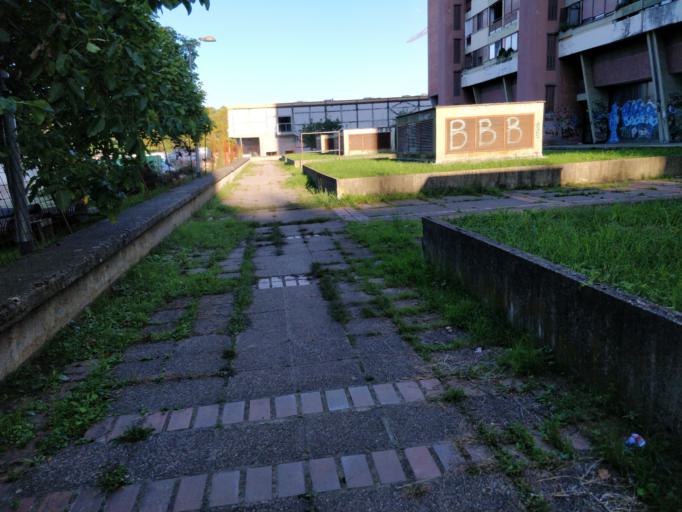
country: HR
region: Grad Zagreb
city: Novi Zagreb
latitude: 45.7807
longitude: 15.9870
